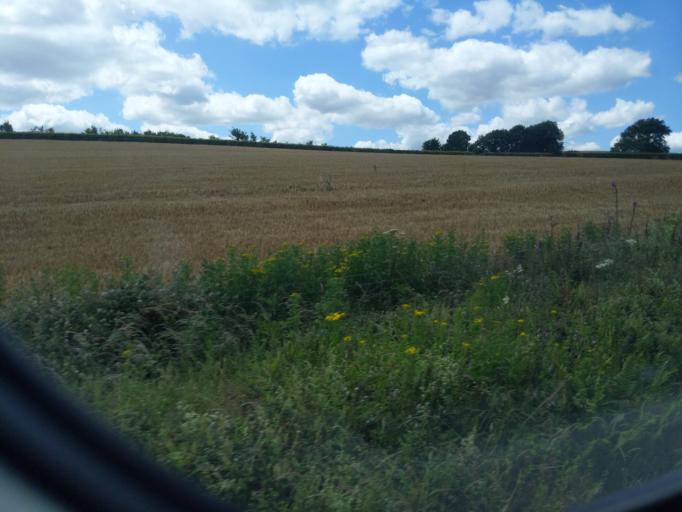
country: GB
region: England
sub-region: Cornwall
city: Liskeard
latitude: 50.4334
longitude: -4.4352
